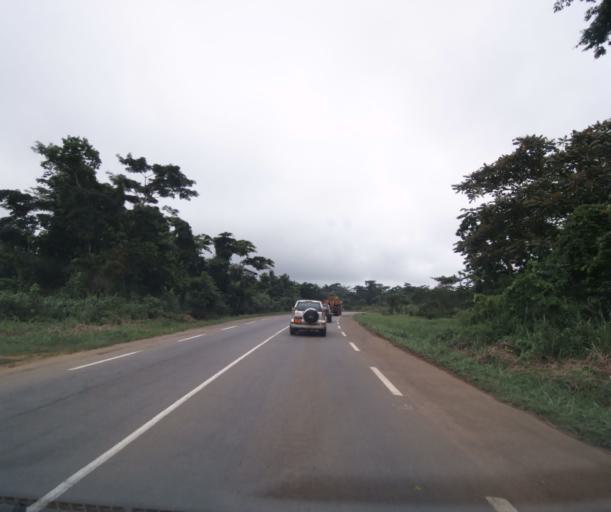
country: CM
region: Centre
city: Mbankomo
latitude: 3.7660
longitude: 11.1337
